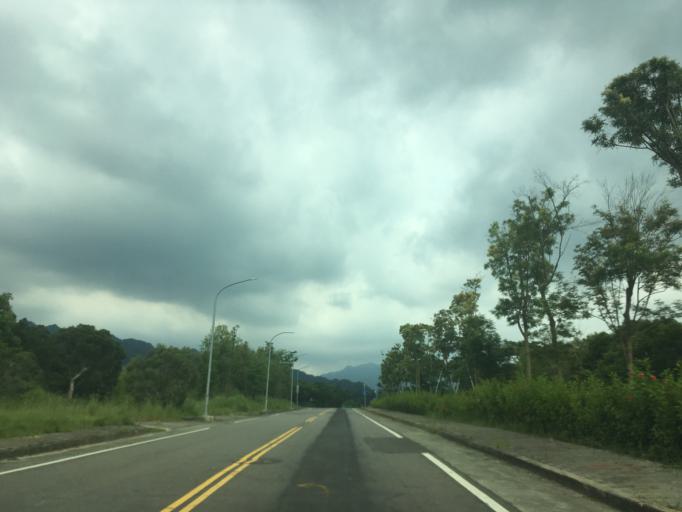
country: TW
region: Taiwan
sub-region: Taichung City
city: Taichung
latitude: 24.1754
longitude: 120.7708
